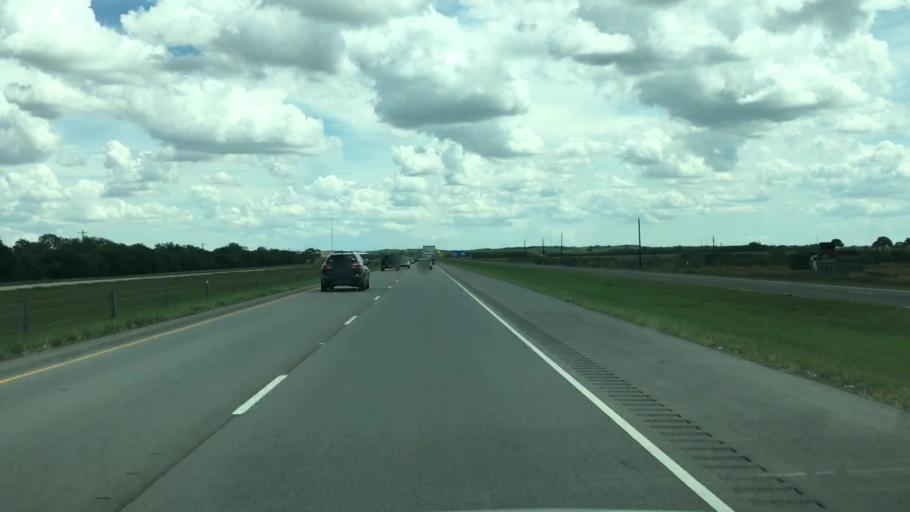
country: US
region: Texas
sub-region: Live Oak County
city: George West
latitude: 28.2714
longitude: -97.9447
